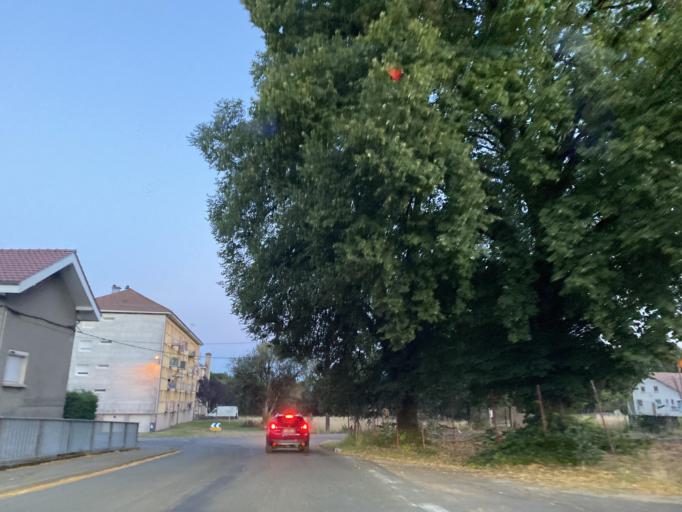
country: FR
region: Franche-Comte
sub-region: Territoire de Belfort
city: Giromagny
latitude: 47.7392
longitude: 6.8237
